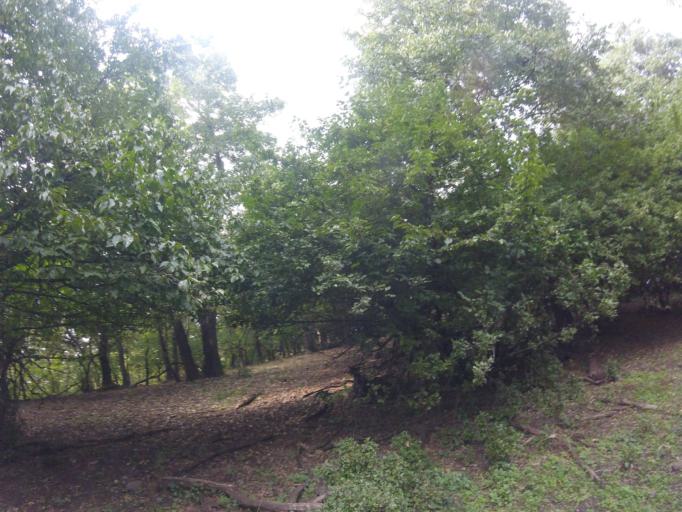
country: HU
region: Komarom-Esztergom
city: Pilismarot
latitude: 47.7873
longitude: 18.8142
